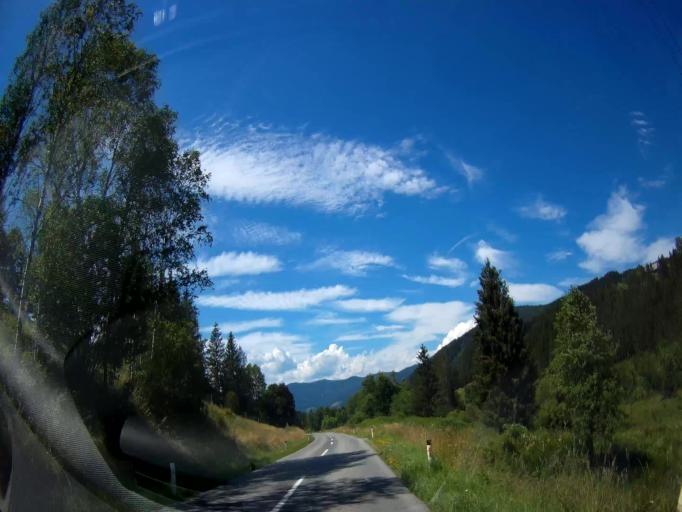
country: AT
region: Carinthia
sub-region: Politischer Bezirk Sankt Veit an der Glan
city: Glodnitz
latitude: 46.8571
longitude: 14.1327
